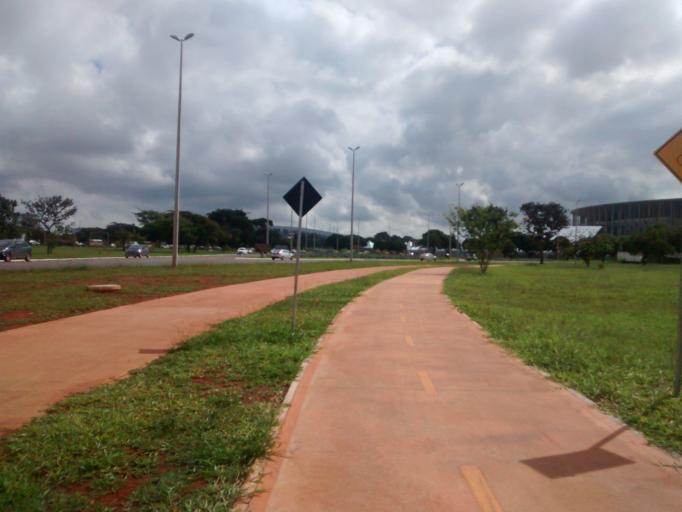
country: BR
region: Federal District
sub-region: Brasilia
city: Brasilia
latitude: -15.7874
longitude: -47.8928
